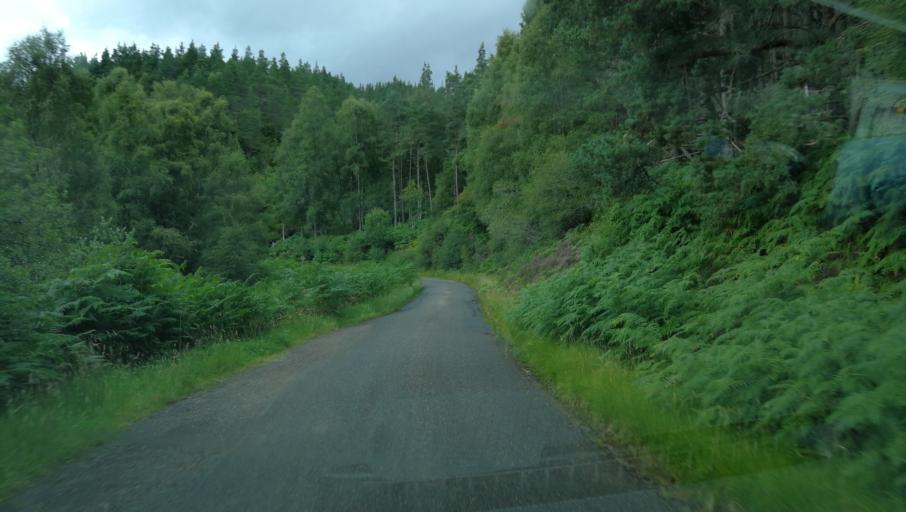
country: GB
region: Scotland
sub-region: Highland
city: Spean Bridge
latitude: 57.2983
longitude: -4.9021
